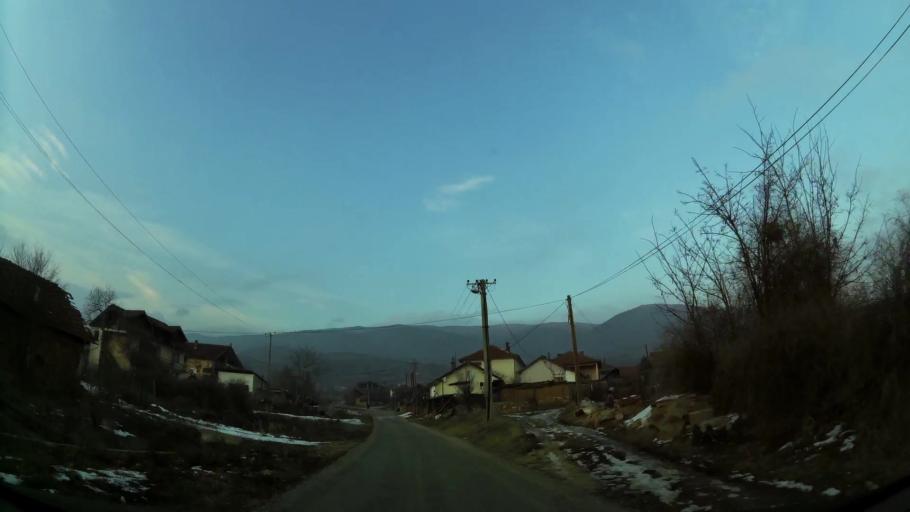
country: MK
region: Aracinovo
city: Arachinovo
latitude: 42.0319
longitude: 21.5484
